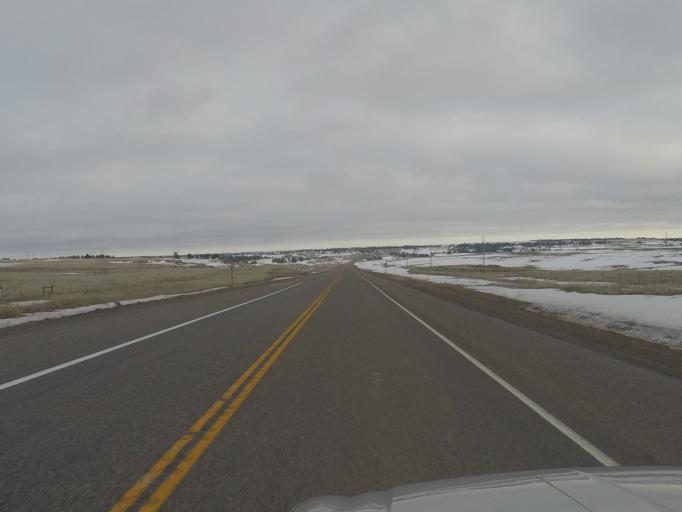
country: US
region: Montana
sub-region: Yellowstone County
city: Billings
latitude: 45.8560
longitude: -108.6501
